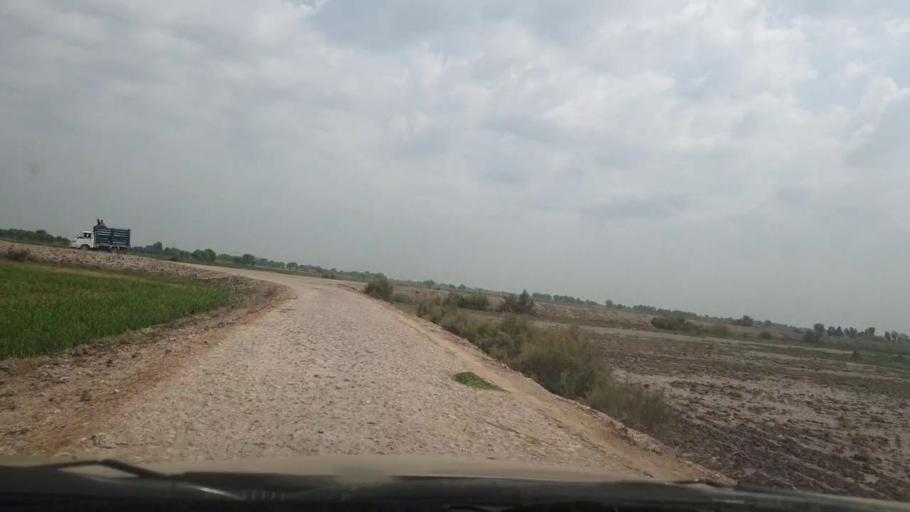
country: PK
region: Sindh
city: Ratodero
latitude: 27.7227
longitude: 68.2328
